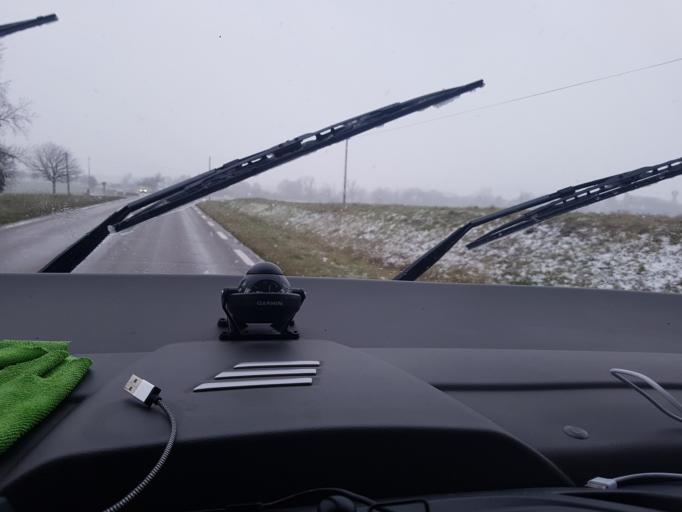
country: FR
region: Lorraine
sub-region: Departement de la Moselle
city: Vic-sur-Seille
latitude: 48.7855
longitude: 6.5662
